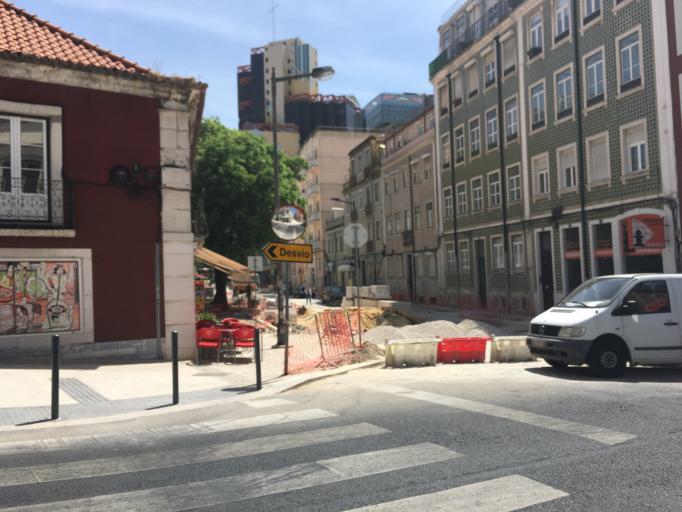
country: PT
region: Lisbon
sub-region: Lisbon
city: Lisbon
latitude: 38.7257
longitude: -9.1627
